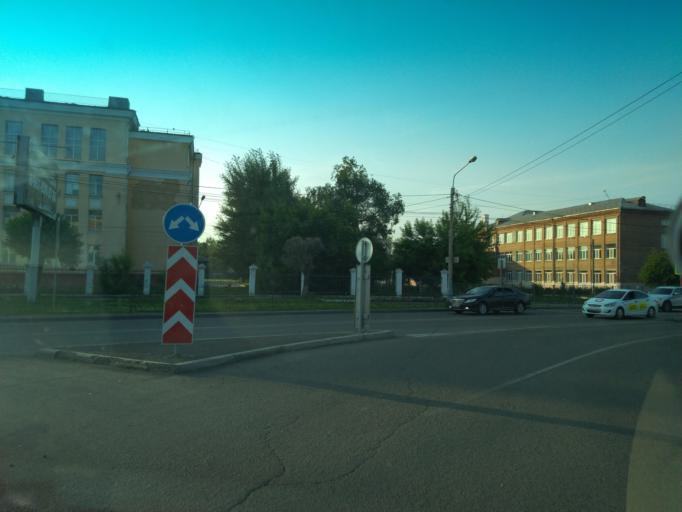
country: RU
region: Krasnoyarskiy
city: Krasnoyarsk
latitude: 56.0025
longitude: 92.9501
